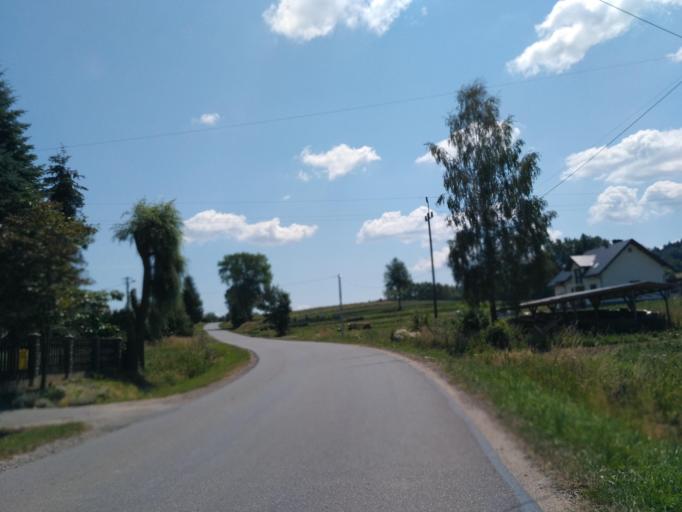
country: PL
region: Subcarpathian Voivodeship
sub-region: Powiat sanocki
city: Niebieszczany
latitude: 49.4941
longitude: 22.1698
